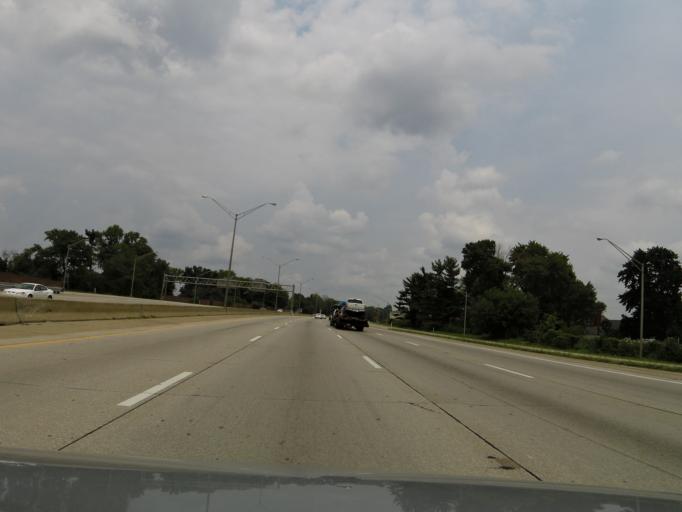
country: US
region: Kentucky
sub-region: Jefferson County
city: Audubon Park
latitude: 38.1967
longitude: -85.7056
